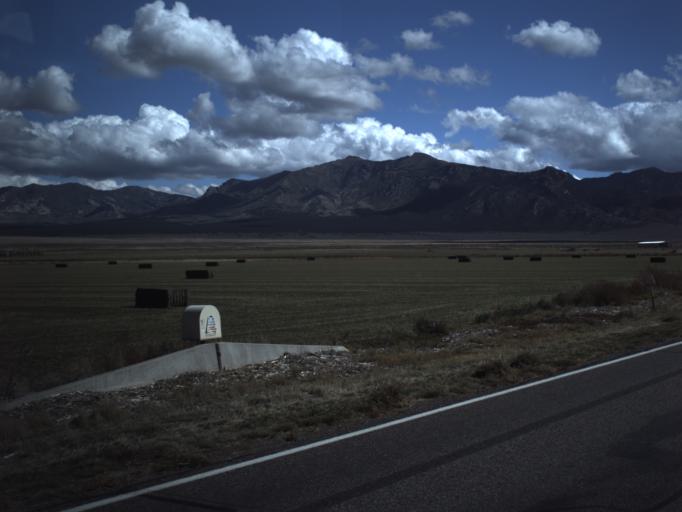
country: US
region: Utah
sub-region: Beaver County
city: Milford
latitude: 38.3606
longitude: -112.9906
